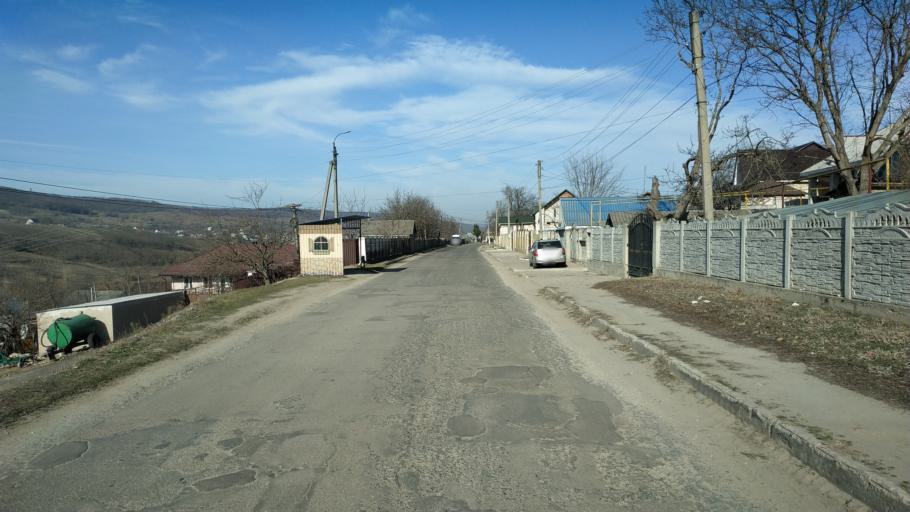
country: MD
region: Chisinau
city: Vatra
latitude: 47.0216
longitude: 28.6443
